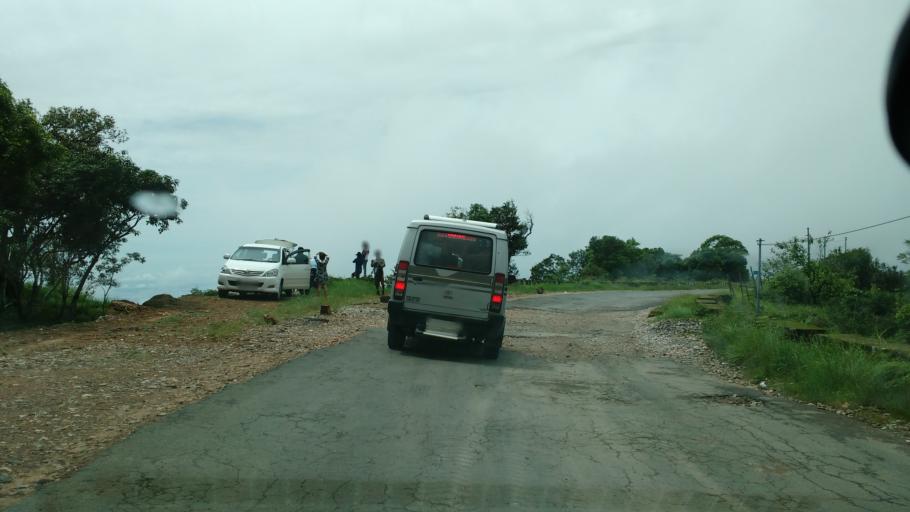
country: IN
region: Meghalaya
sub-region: East Khasi Hills
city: Cherrapunji
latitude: 25.2409
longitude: 91.7325
